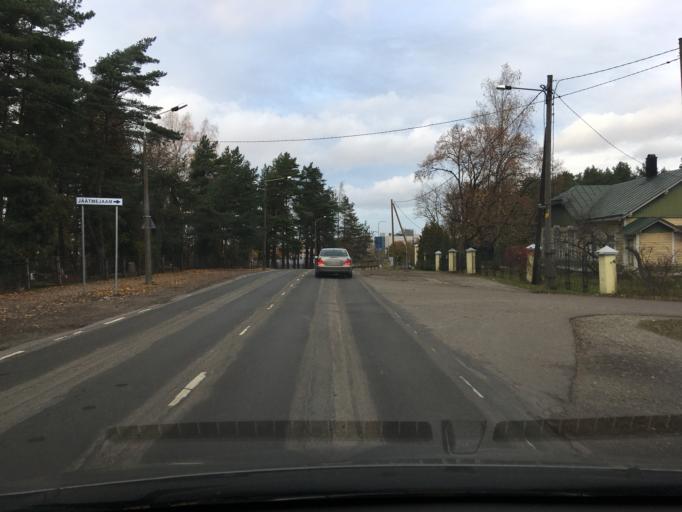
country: EE
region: Harju
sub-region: Tallinna linn
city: Tallinn
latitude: 59.3929
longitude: 24.7085
